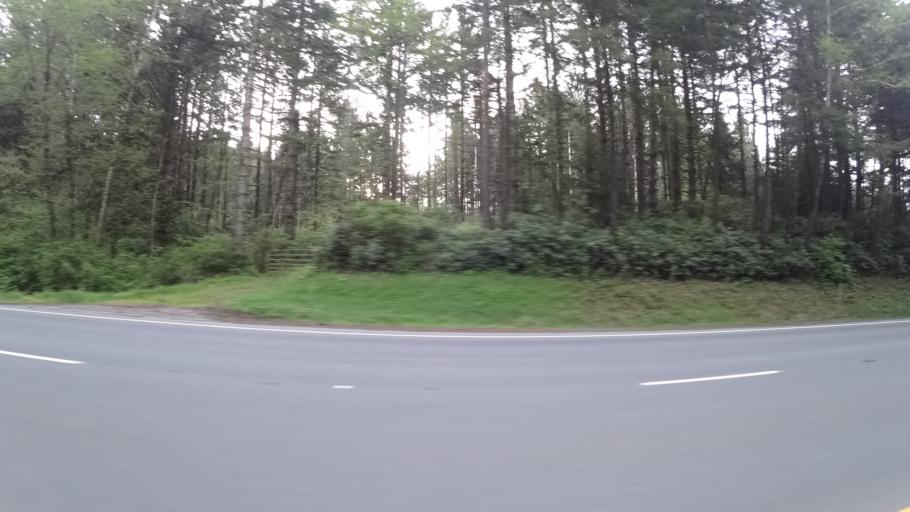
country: US
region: Oregon
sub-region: Coos County
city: Lakeside
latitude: 43.6091
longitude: -124.1807
